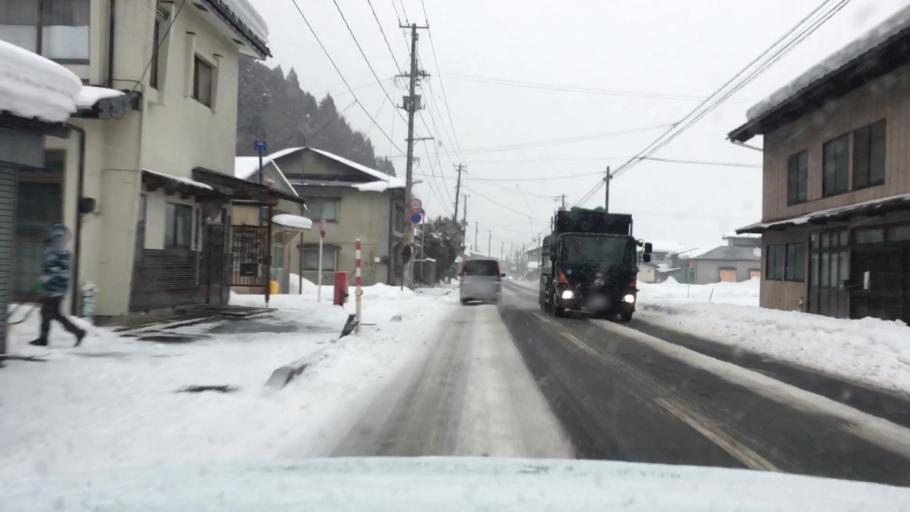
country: JP
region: Iwate
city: Ichinohe
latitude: 40.0937
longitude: 141.0470
